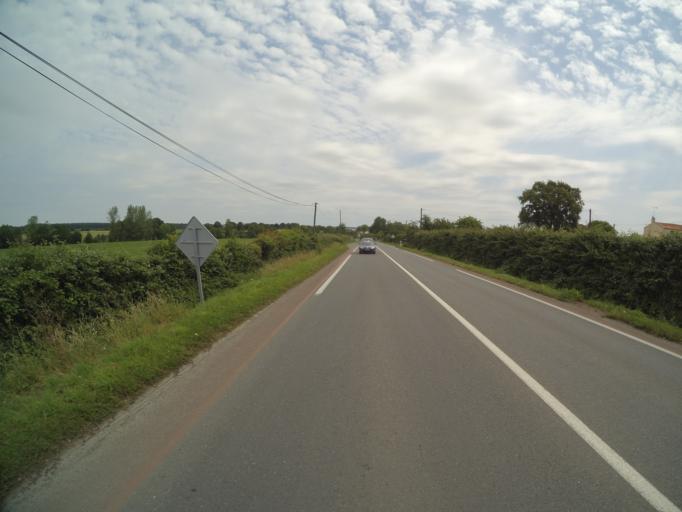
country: FR
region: Pays de la Loire
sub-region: Departement de la Vendee
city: Les Herbiers
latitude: 46.8505
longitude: -1.0605
